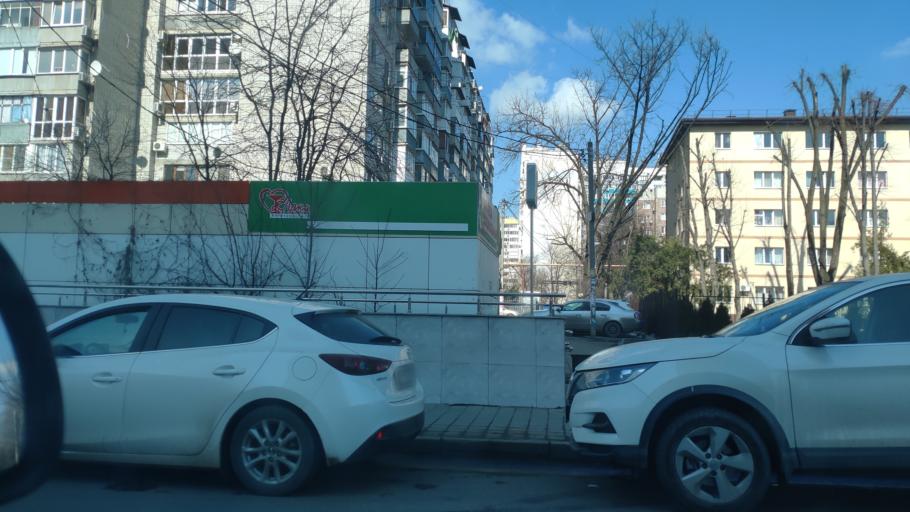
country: RU
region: Krasnodarskiy
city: Krasnodar
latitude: 45.0556
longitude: 39.0092
